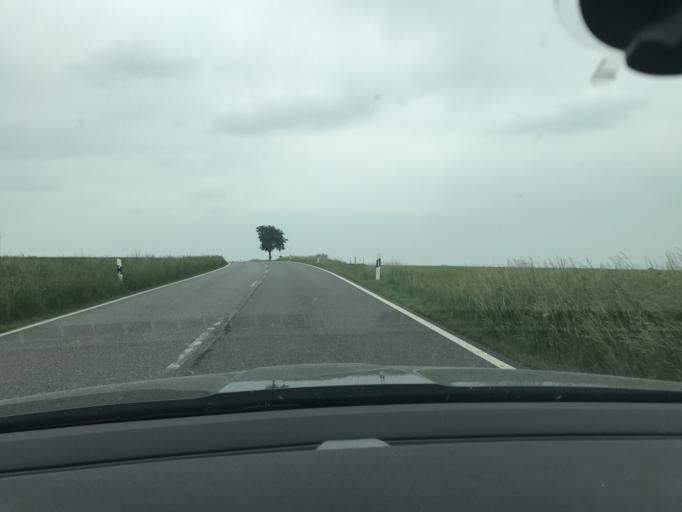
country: DE
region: Saxony
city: Meissen
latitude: 51.1460
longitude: 13.4346
